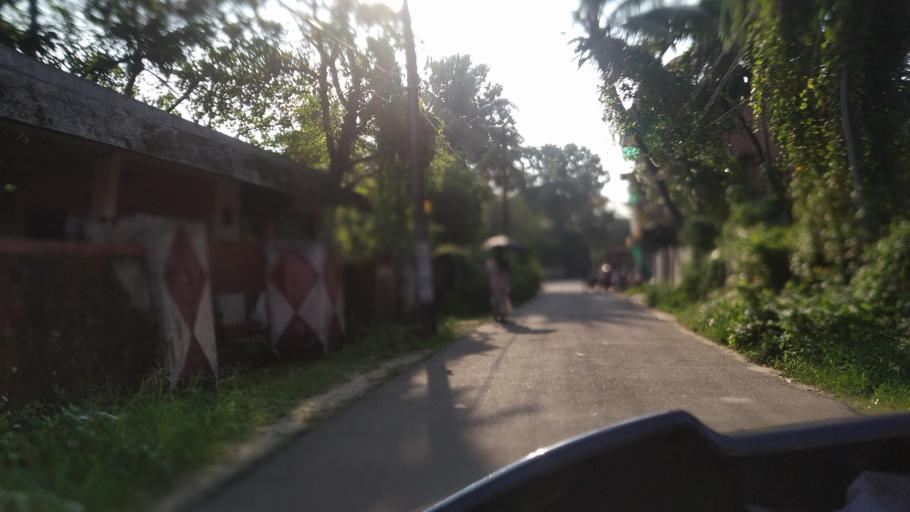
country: IN
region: Kerala
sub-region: Ernakulam
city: Elur
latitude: 10.0460
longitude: 76.2212
